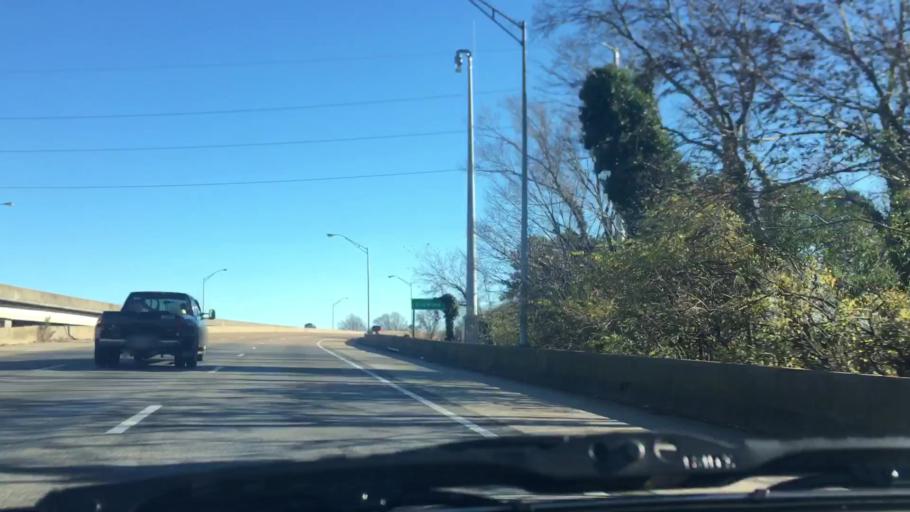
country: US
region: Virginia
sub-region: City of Hampton
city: East Hampton
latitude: 37.0296
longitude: -76.3347
